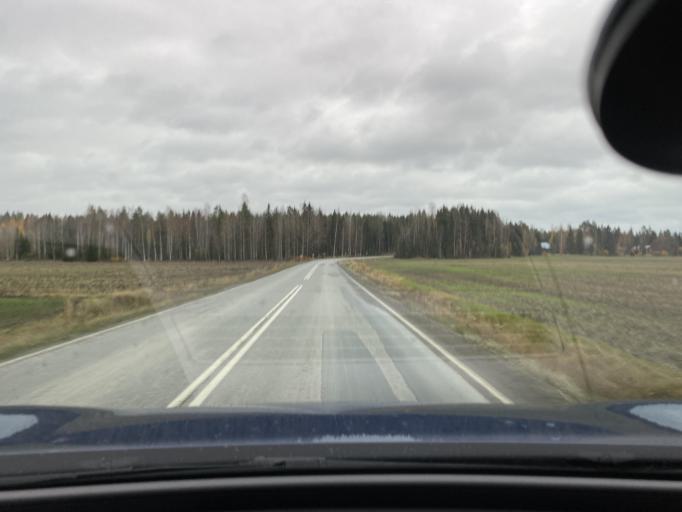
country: FI
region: Satakunta
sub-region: Pori
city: Huittinen
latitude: 61.1454
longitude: 22.6298
